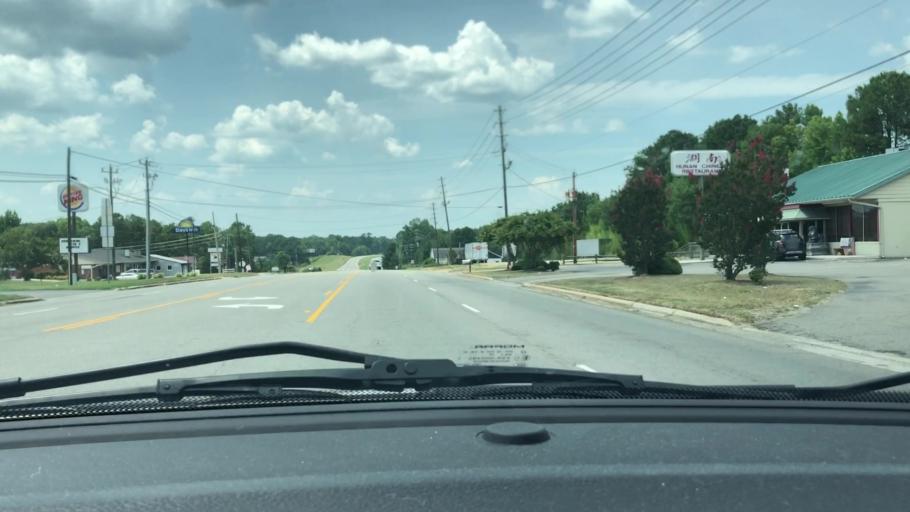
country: US
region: North Carolina
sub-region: Lee County
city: Sanford
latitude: 35.4970
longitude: -79.1978
